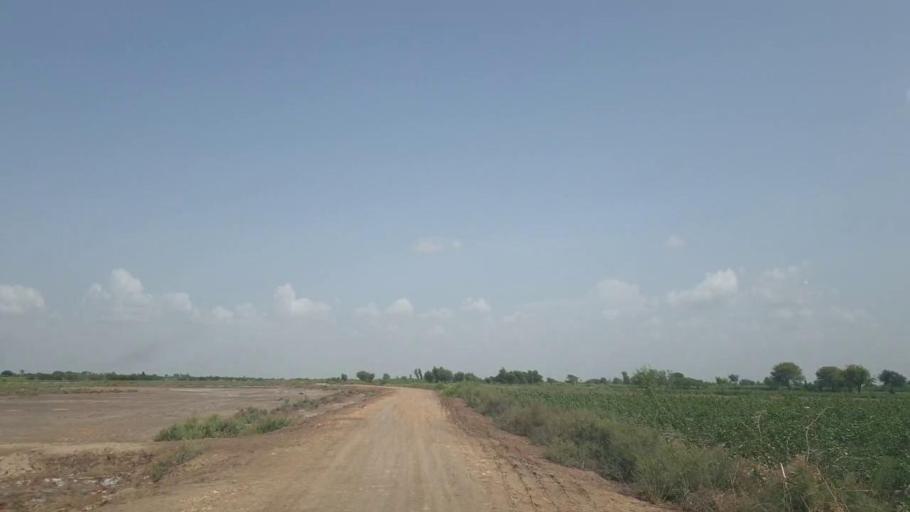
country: PK
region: Sindh
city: Tando Bago
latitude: 24.7550
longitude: 69.1721
